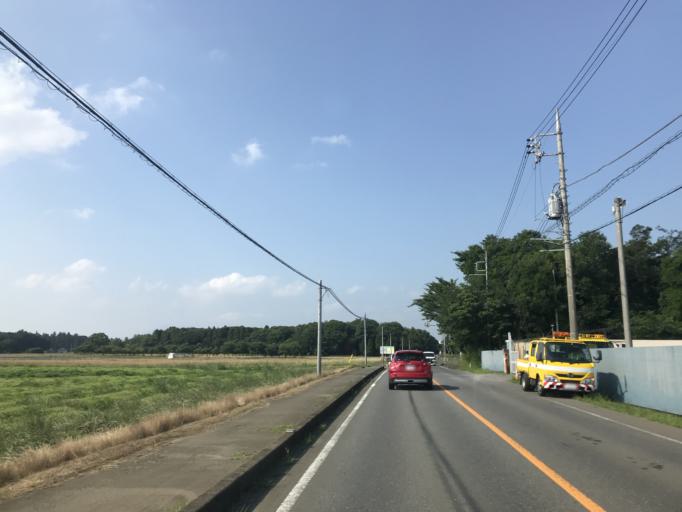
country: JP
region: Ibaraki
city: Naka
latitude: 36.0609
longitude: 140.0917
